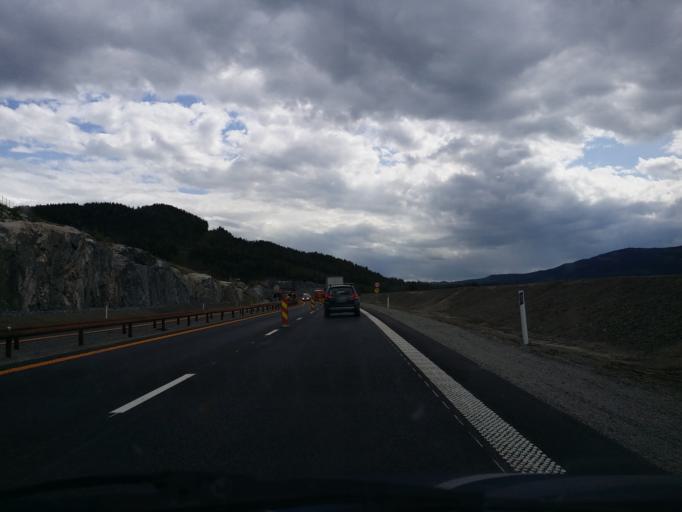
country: NO
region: Akershus
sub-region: Eidsvoll
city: Eidsvoll
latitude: 60.4471
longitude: 11.2423
